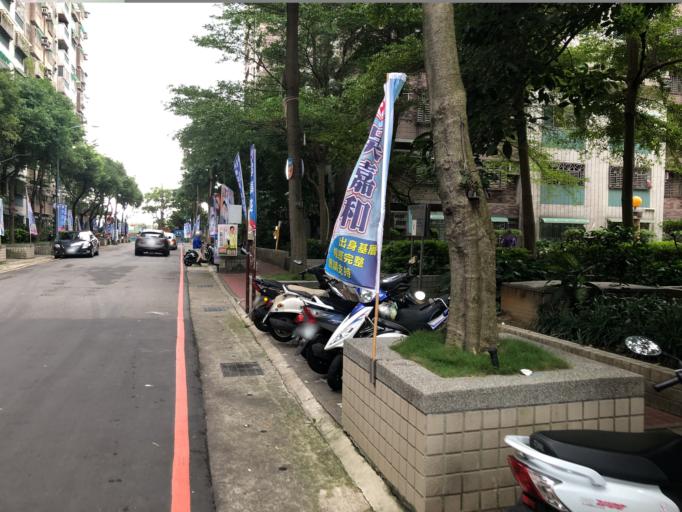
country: TW
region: Taiwan
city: Taoyuan City
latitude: 24.9664
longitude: 121.2518
